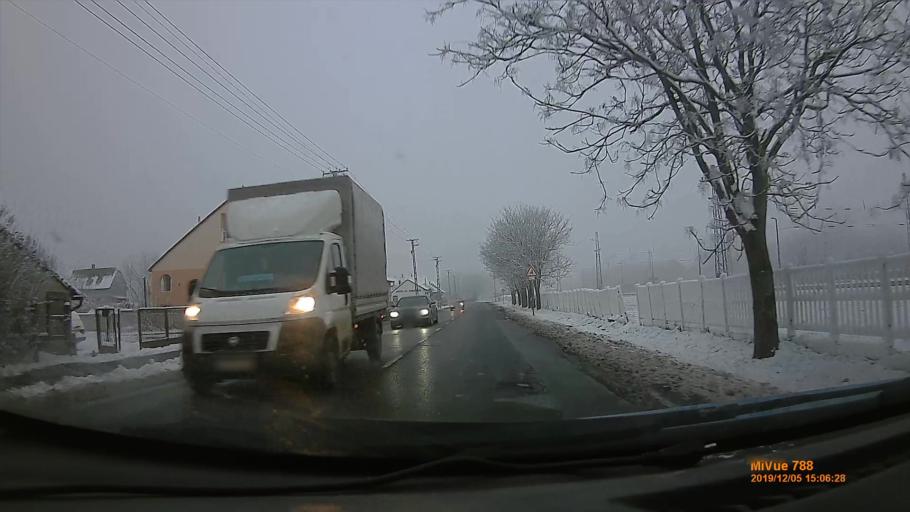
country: HU
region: Szabolcs-Szatmar-Bereg
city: Rakamaz
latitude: 48.1180
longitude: 21.4774
